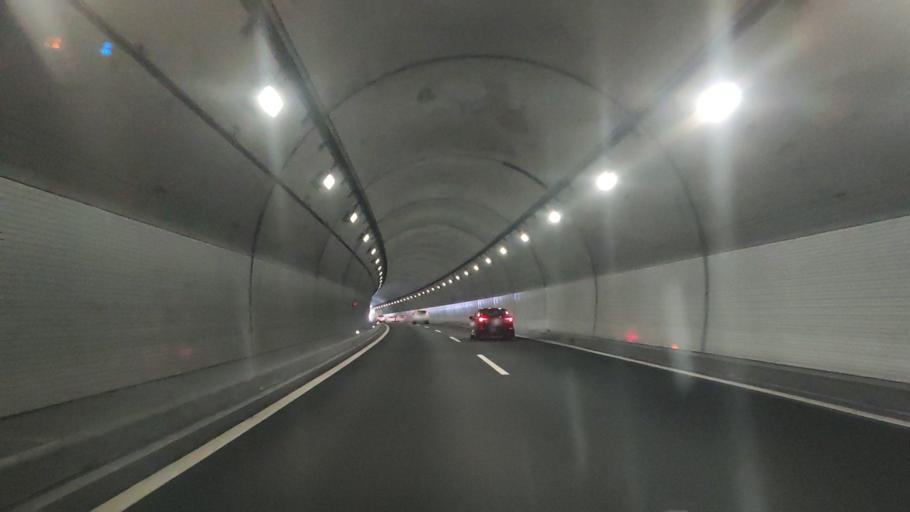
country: JP
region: Fukuoka
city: Kanda
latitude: 33.8039
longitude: 130.9411
